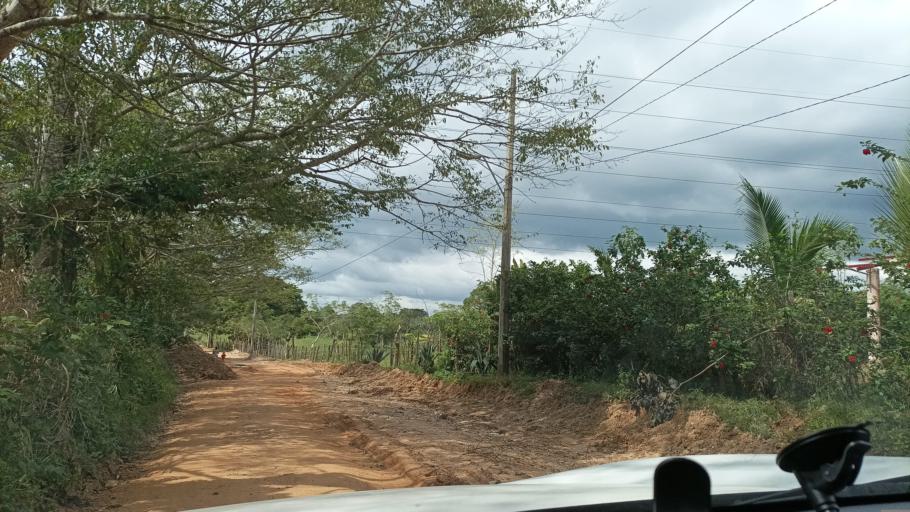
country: MX
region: Veracruz
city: Soconusco
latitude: 17.9666
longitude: -94.8863
